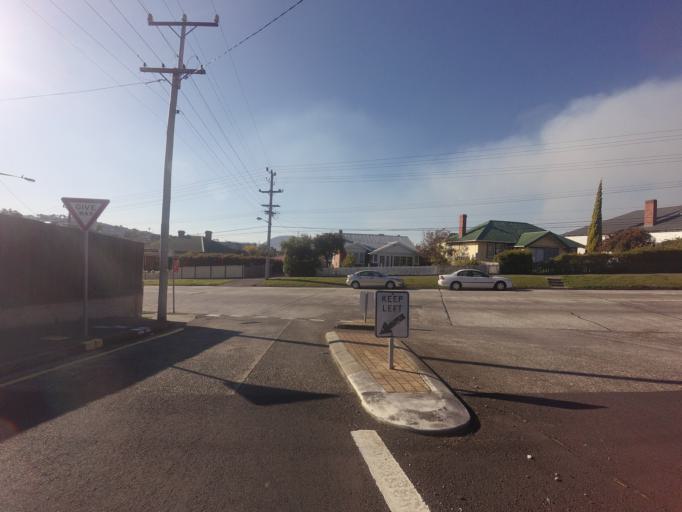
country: AU
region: Tasmania
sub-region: Hobart
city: New Town
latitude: -42.8650
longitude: 147.2942
